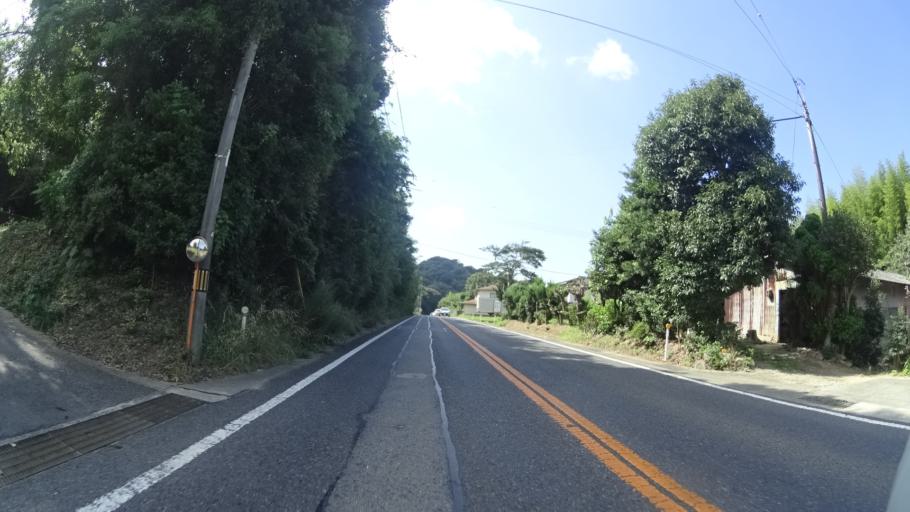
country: JP
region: Yamaguchi
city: Shimonoseki
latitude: 34.0971
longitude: 130.9001
